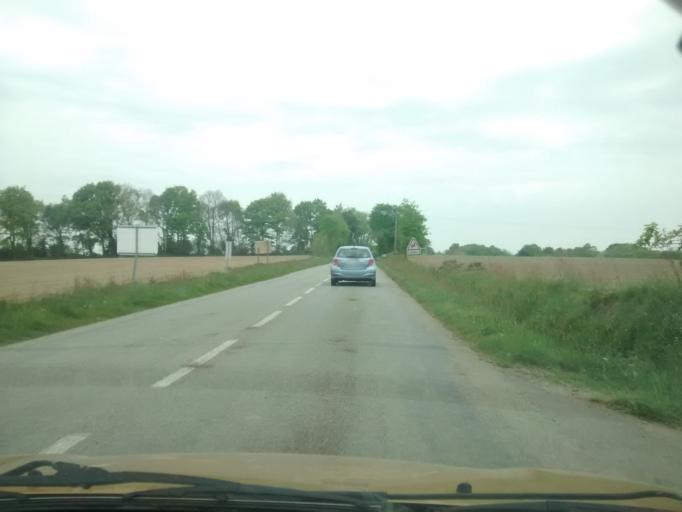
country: FR
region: Brittany
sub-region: Departement du Morbihan
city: Berric
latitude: 47.6373
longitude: -2.5149
